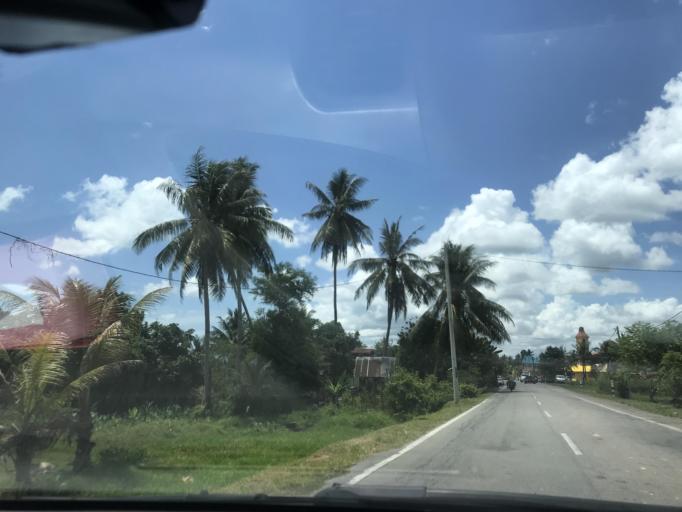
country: MY
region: Kelantan
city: Tumpat
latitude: 6.2065
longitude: 102.1164
